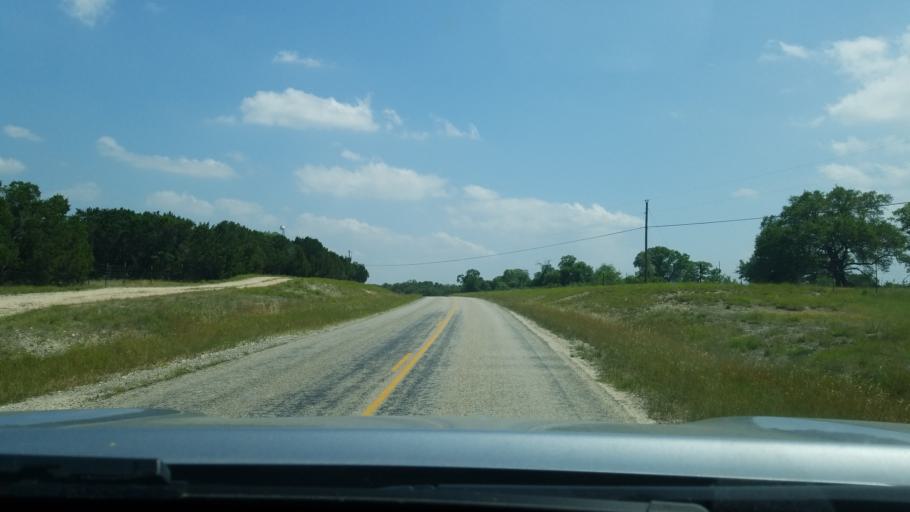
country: US
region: Texas
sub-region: Bexar County
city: Fair Oaks Ranch
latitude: 29.9074
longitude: -98.5687
